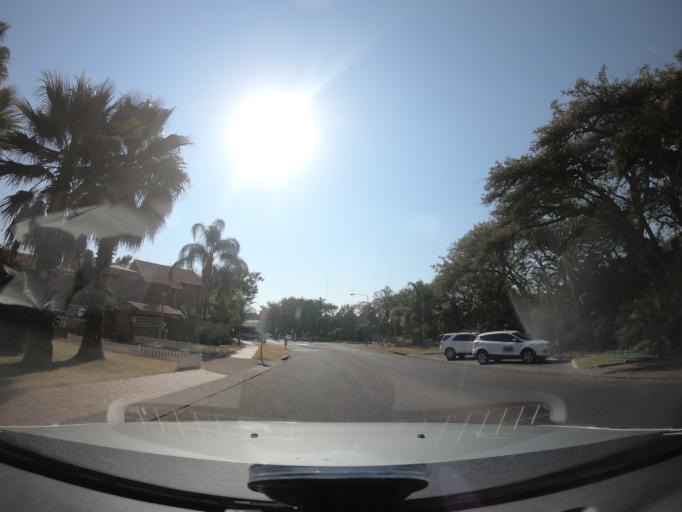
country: ZA
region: Gauteng
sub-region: City of Tshwane Metropolitan Municipality
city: Pretoria
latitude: -25.7762
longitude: 28.3362
